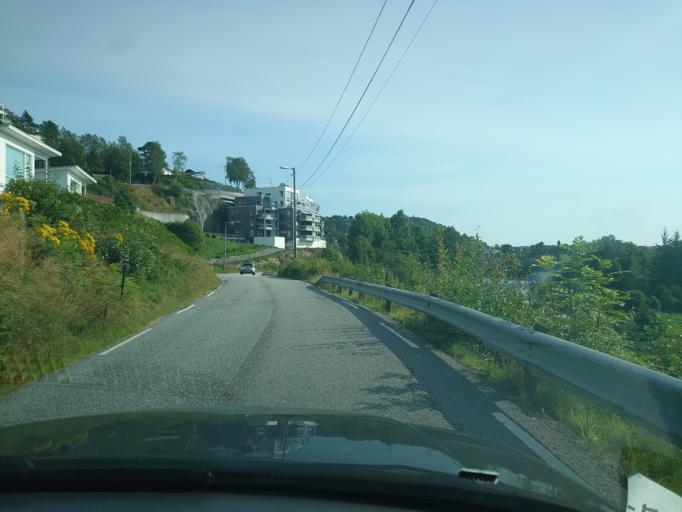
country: NO
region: Hordaland
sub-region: Bergen
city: Ytrebygda
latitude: 60.3406
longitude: 5.2817
